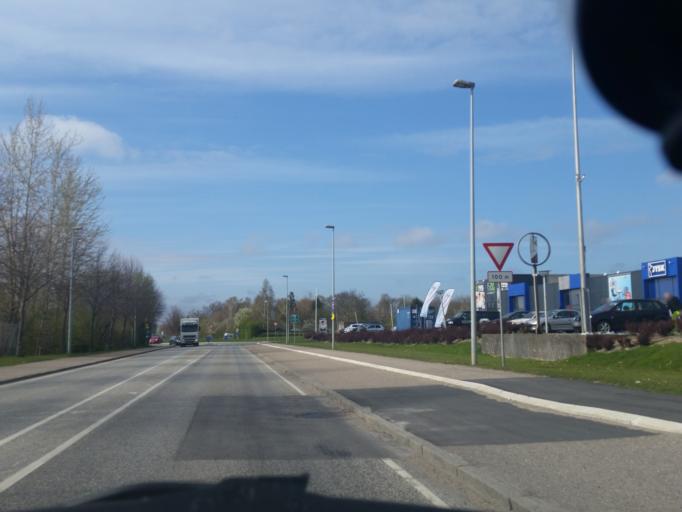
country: DK
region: Zealand
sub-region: Soro Kommune
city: Soro
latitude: 55.4442
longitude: 11.5649
